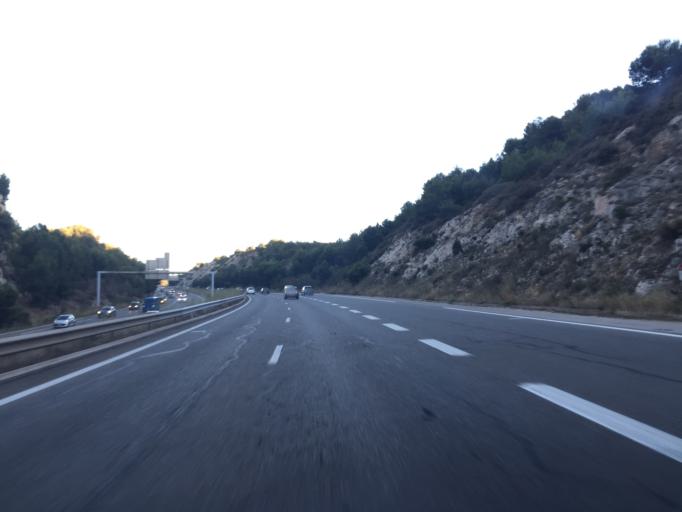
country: FR
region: Provence-Alpes-Cote d'Azur
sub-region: Departement des Bouches-du-Rhone
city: Les Pennes-Mirabeau
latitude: 43.3936
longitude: 5.2994
